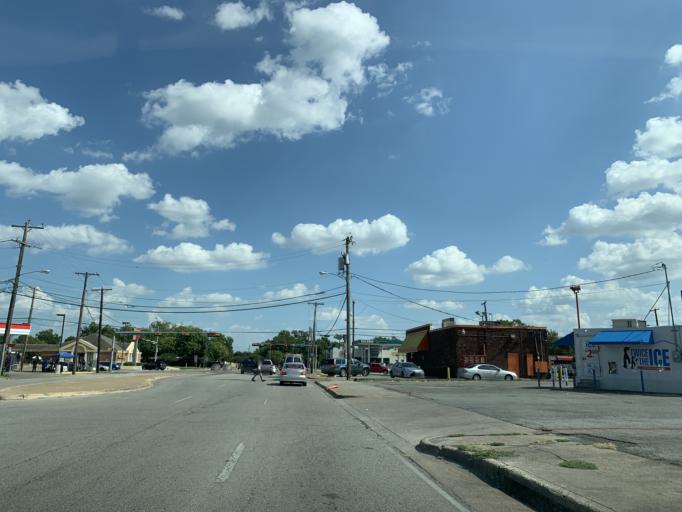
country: US
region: Texas
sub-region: Dallas County
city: Hutchins
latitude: 32.6953
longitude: -96.7727
